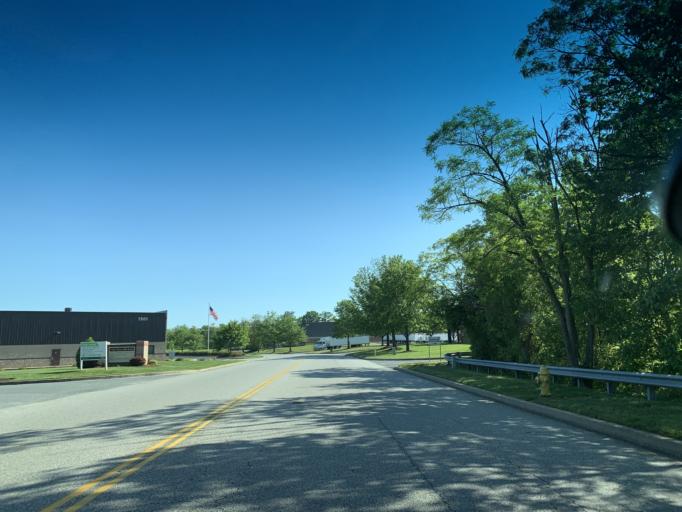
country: US
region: Maryland
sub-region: Harford County
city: Riverside
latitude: 39.4853
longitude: -76.2342
